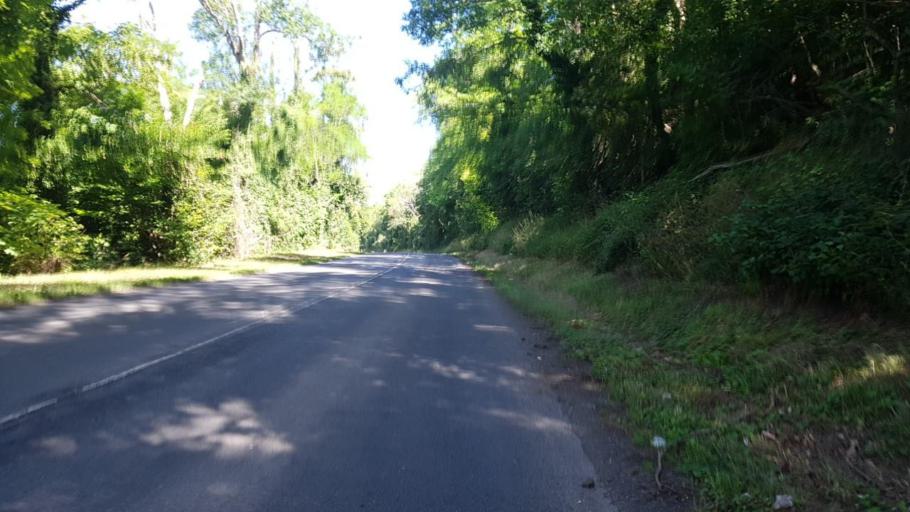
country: FR
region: Picardie
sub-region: Departement de l'Aisne
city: Charly-sur-Marne
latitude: 48.9752
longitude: 3.2515
